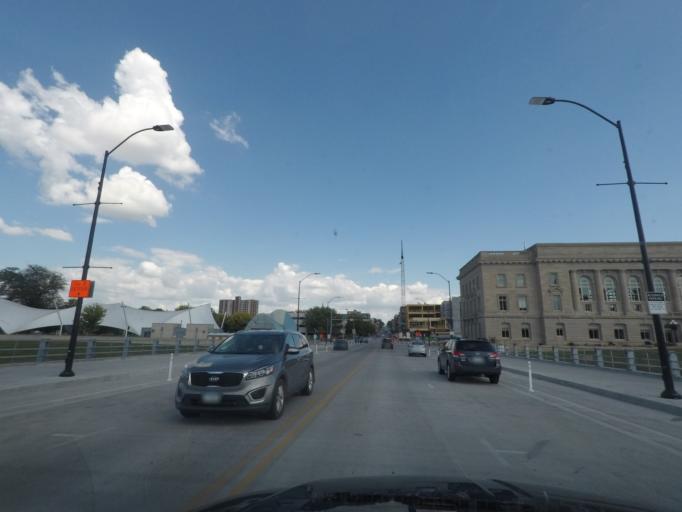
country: US
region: Iowa
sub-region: Polk County
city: Des Moines
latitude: 41.5894
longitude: -93.6176
